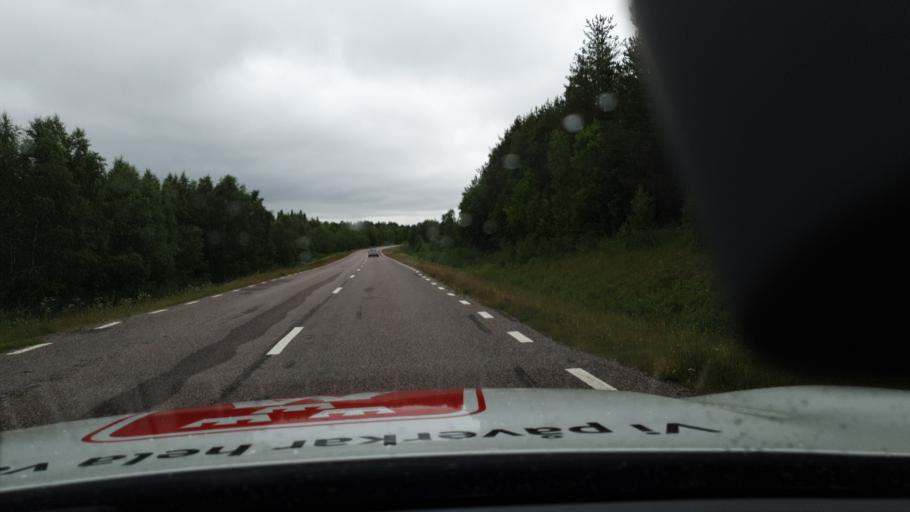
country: FI
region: Lapland
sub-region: Torniolaakso
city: Pello
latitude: 66.9940
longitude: 23.7714
